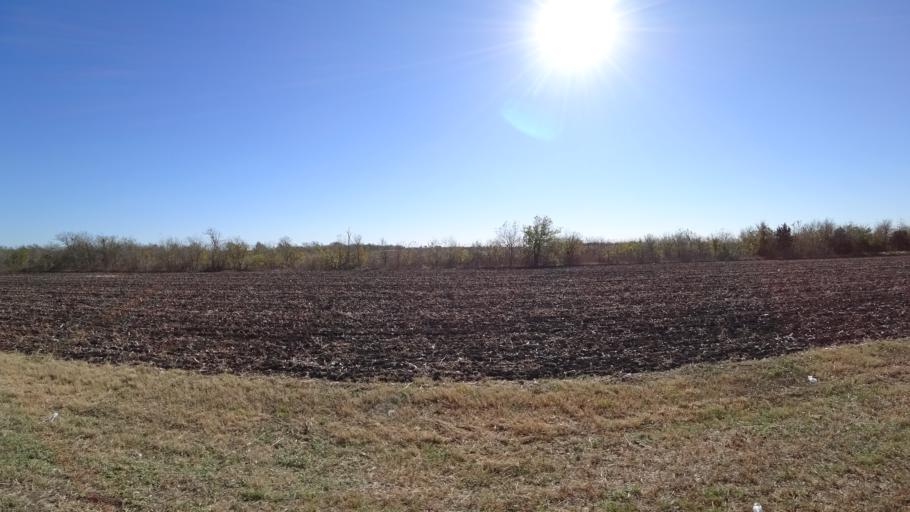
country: US
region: Texas
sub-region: Travis County
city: Garfield
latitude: 30.0988
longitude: -97.6565
